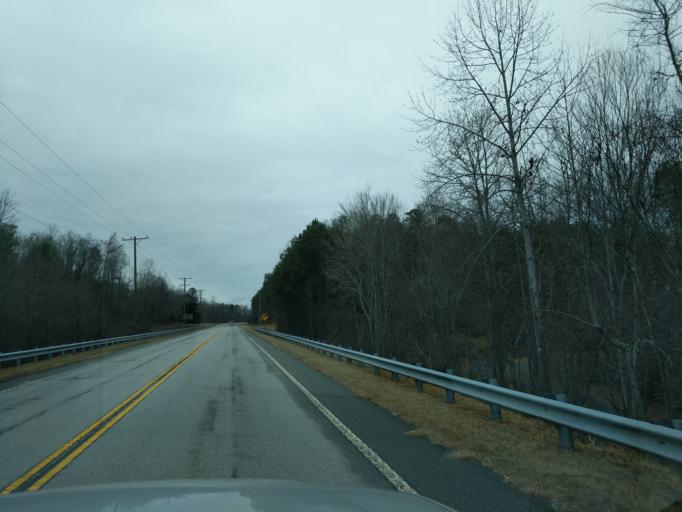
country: US
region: South Carolina
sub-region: Pickens County
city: Pickens
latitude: 34.9178
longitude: -82.9105
